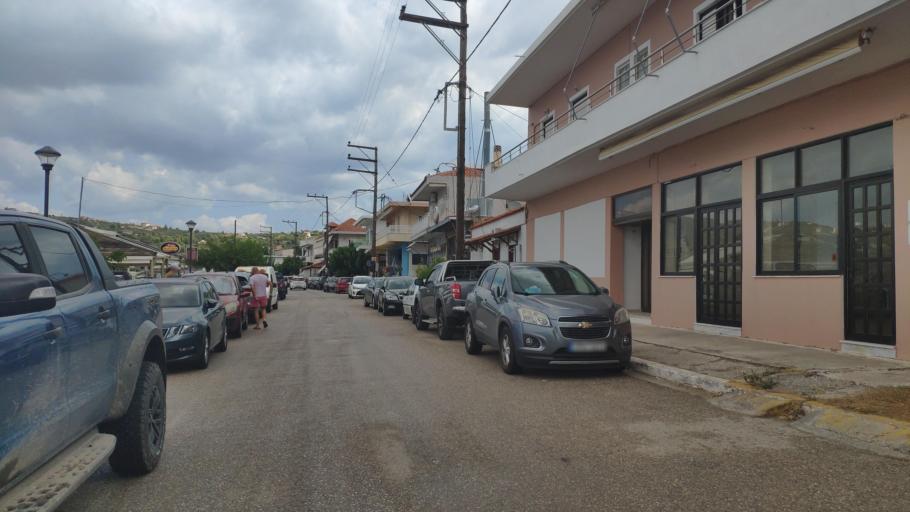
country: GR
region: Central Greece
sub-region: Nomos Fthiotidos
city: Malesina
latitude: 38.6530
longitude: 23.1923
